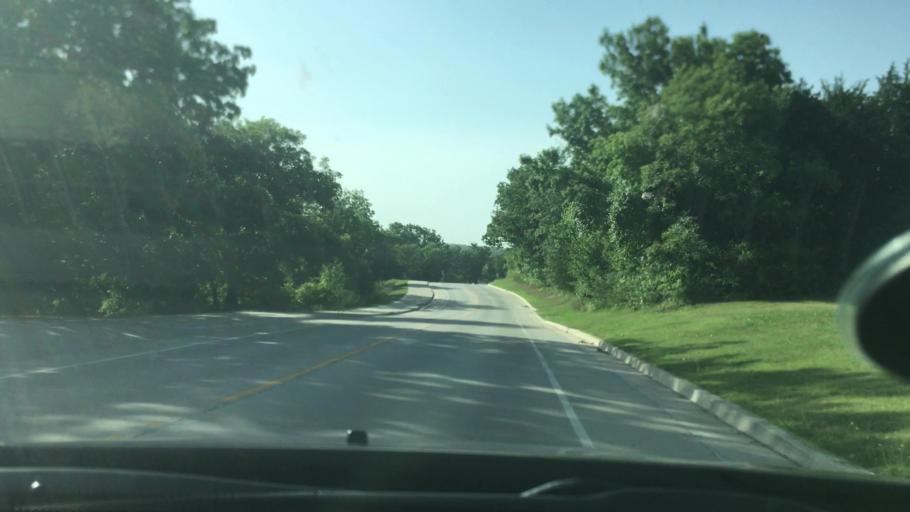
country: US
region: Oklahoma
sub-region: Pontotoc County
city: Ada
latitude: 34.7695
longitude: -96.6609
